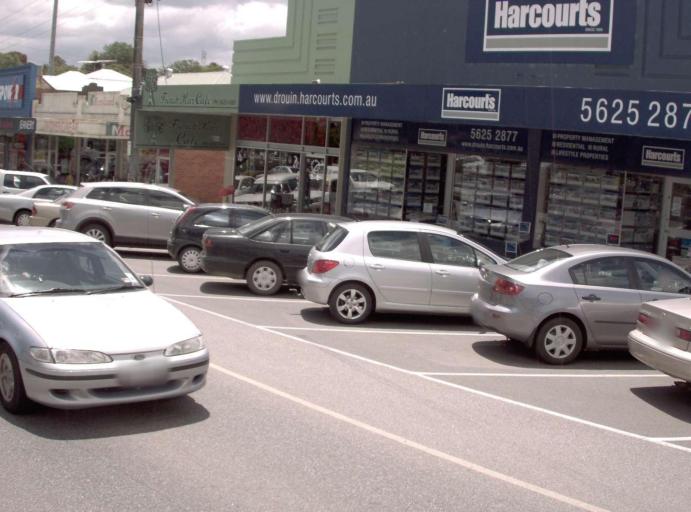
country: AU
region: Victoria
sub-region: Baw Baw
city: Warragul
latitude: -38.1359
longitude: 145.8566
